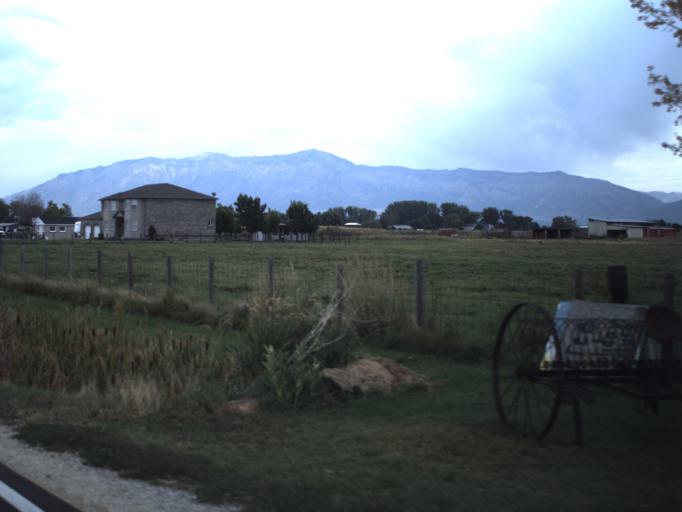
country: US
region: Utah
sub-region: Weber County
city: West Haven
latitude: 41.2290
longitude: -112.0928
